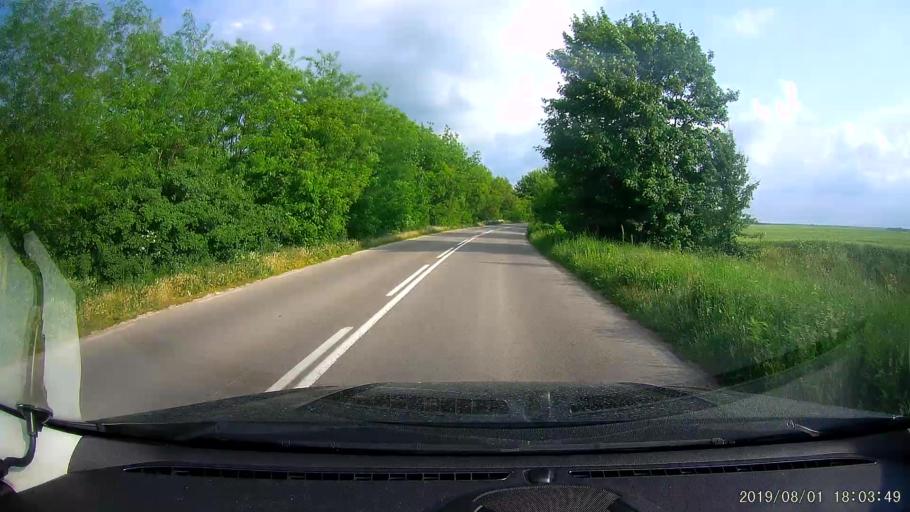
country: BG
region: Silistra
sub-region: Obshtina Alfatar
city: Alfatar
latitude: 43.9186
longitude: 27.2903
